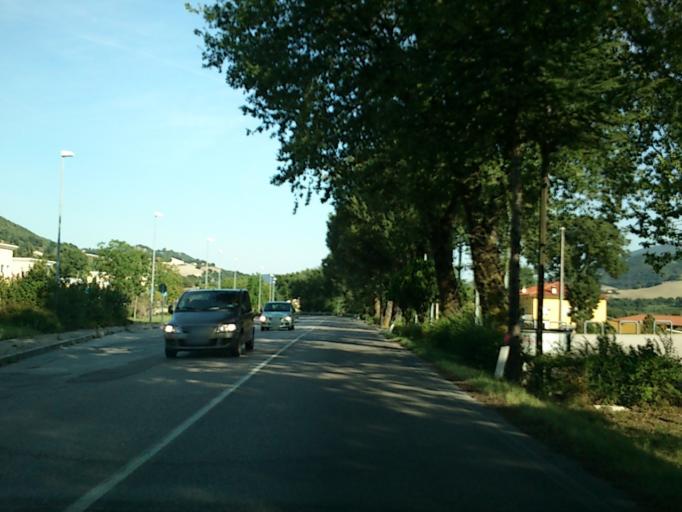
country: IT
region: The Marches
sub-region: Provincia di Pesaro e Urbino
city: Canavaccio
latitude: 43.6925
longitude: 12.7046
